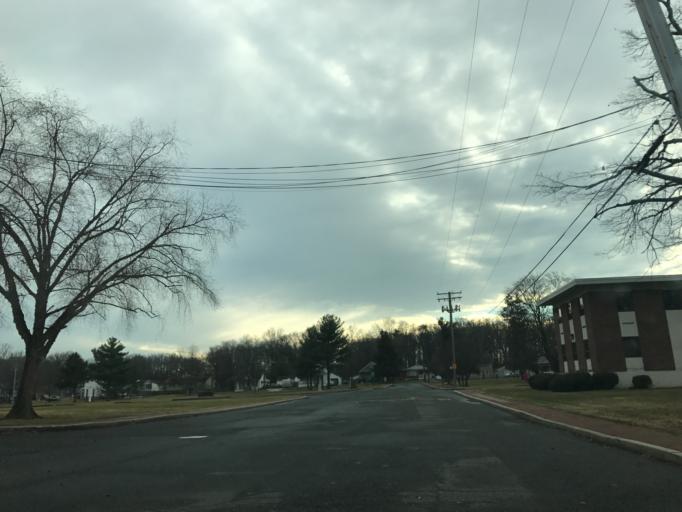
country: US
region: Maryland
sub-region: Baltimore County
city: Essex
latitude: 39.3167
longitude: -76.4697
